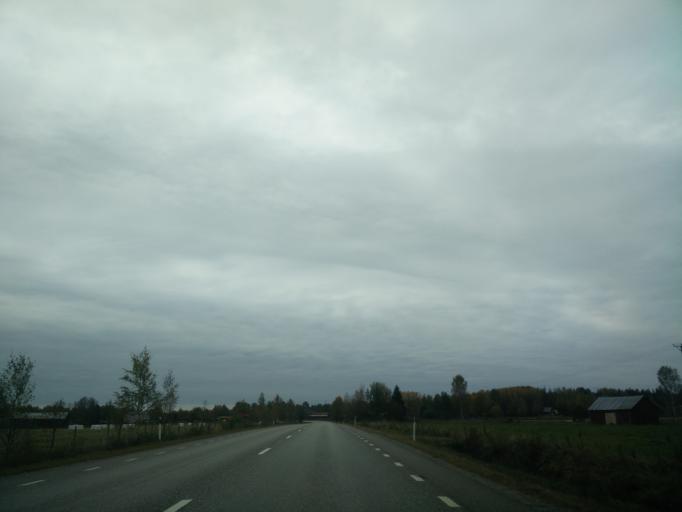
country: SE
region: Gaevleborg
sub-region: Gavle Kommun
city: Norrsundet
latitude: 60.9013
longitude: 17.0515
